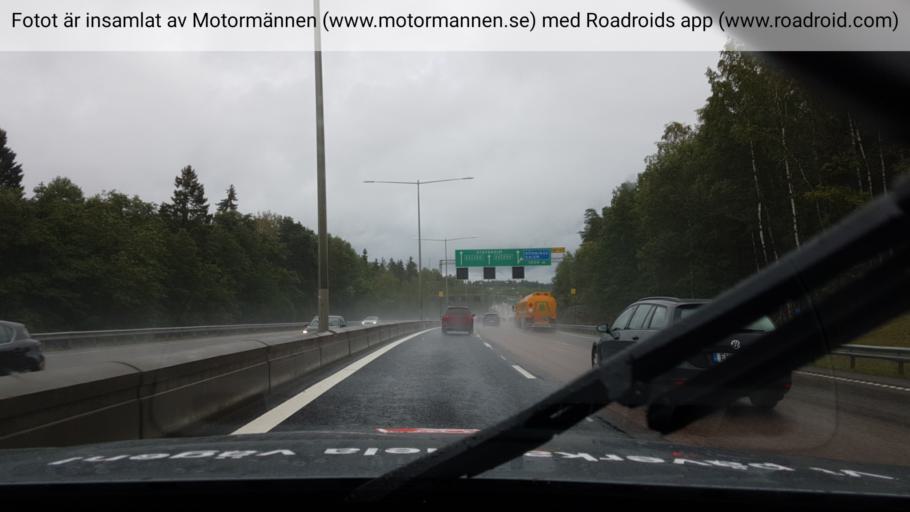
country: SE
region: Stockholm
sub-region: Salems Kommun
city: Ronninge
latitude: 59.2110
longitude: 17.7213
